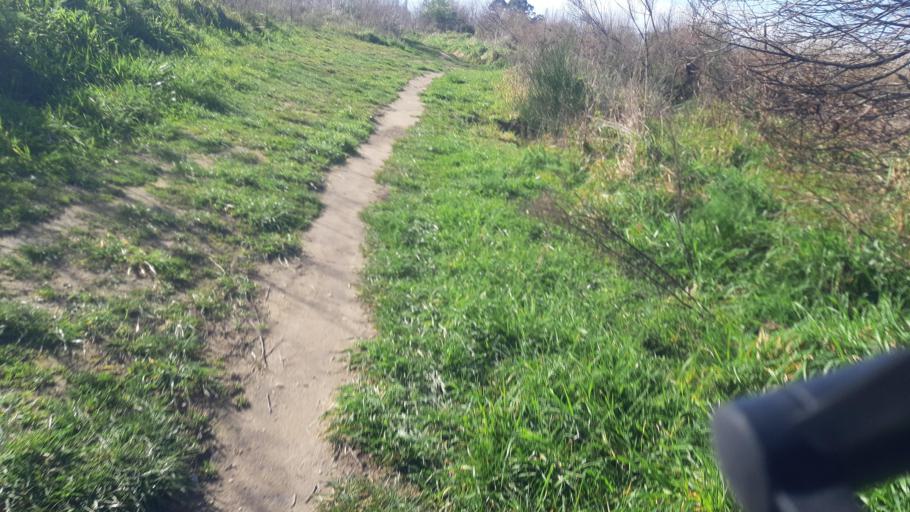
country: NZ
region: Tasman
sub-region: Tasman District
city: Brightwater
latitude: -41.3466
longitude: 173.1152
